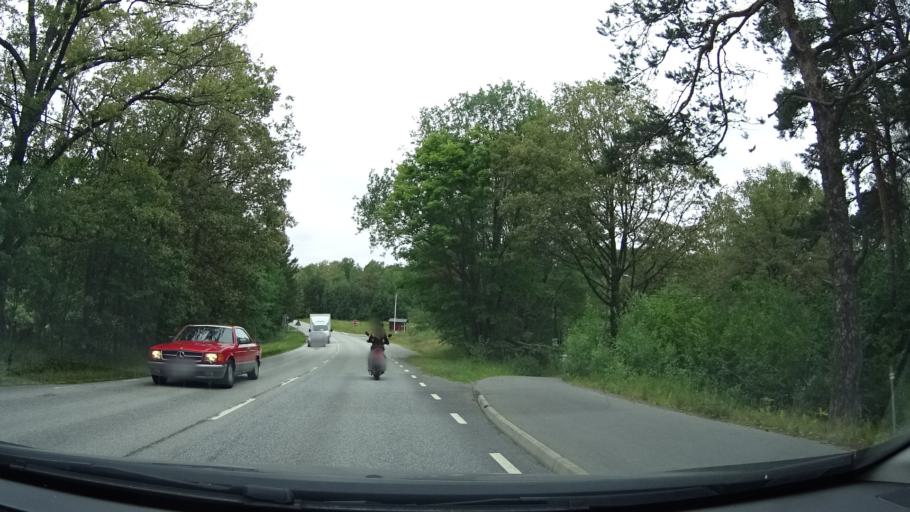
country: SE
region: Stockholm
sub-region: Varmdo Kommun
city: Hemmesta
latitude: 59.3377
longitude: 18.4873
